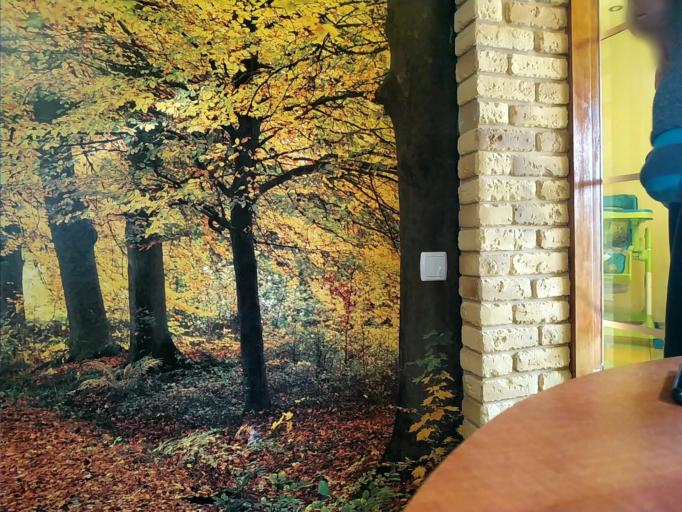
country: RU
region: Novgorod
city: Parfino
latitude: 57.8000
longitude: 31.6140
